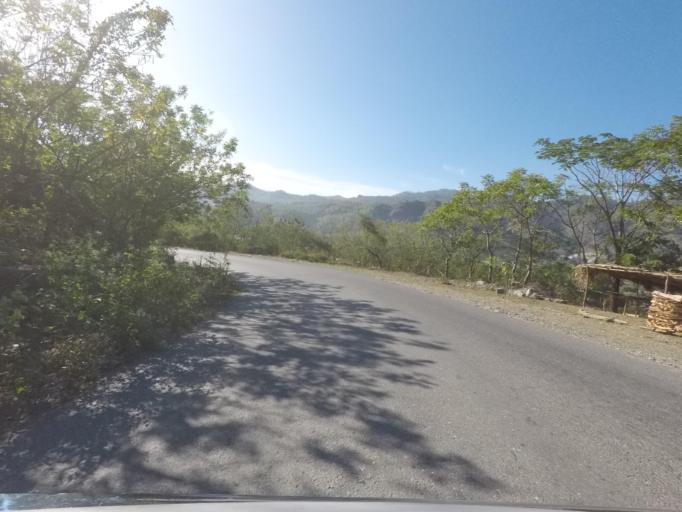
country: TL
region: Dili
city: Dili
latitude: -8.5579
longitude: 125.6435
